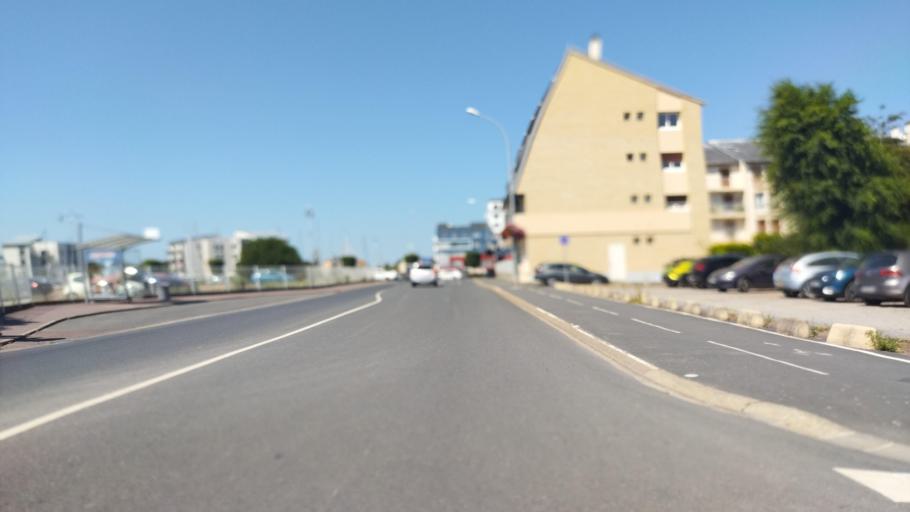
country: FR
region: Lower Normandy
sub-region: Departement du Calvados
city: Courseulles-sur-Mer
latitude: 49.3315
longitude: -0.4626
